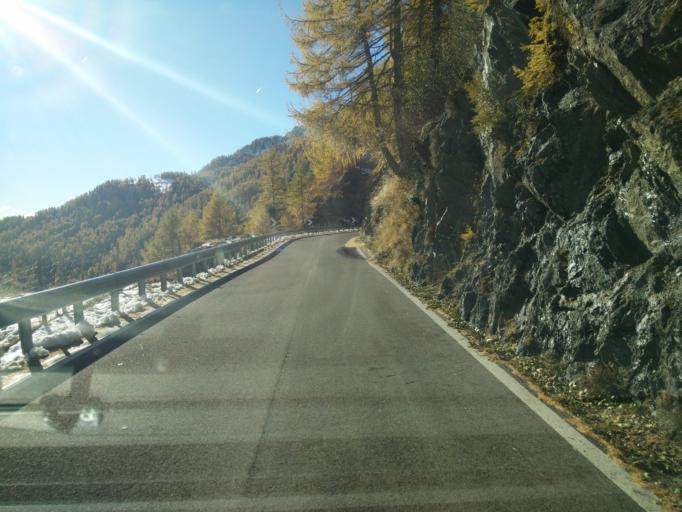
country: IT
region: Trentino-Alto Adige
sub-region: Bolzano
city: Moso in Passiria
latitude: 46.8897
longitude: 11.1272
